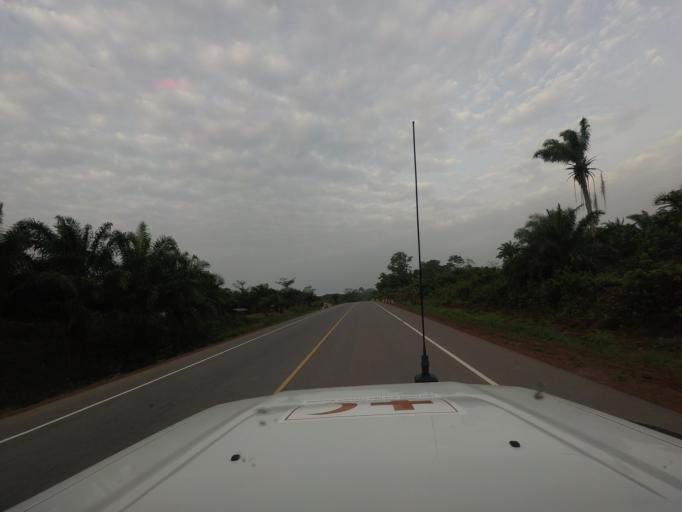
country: LR
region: Nimba
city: Sanniquellie
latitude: 7.1800
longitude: -9.0297
